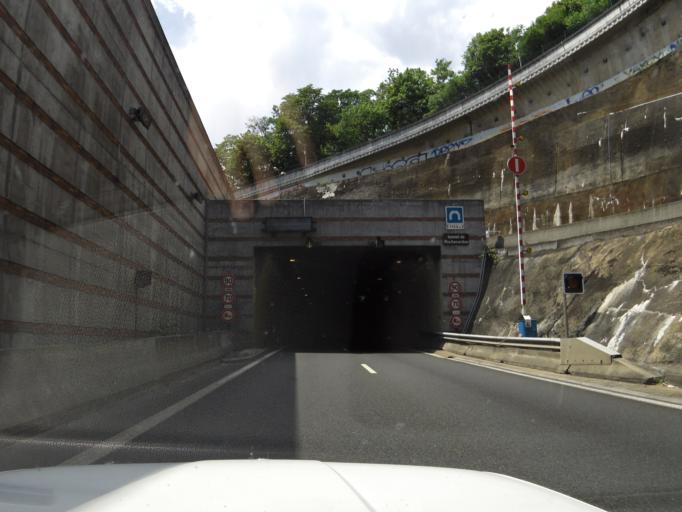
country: FR
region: Rhone-Alpes
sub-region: Departement du Rhone
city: Caluire-et-Cuire
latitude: 45.7906
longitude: 4.8123
